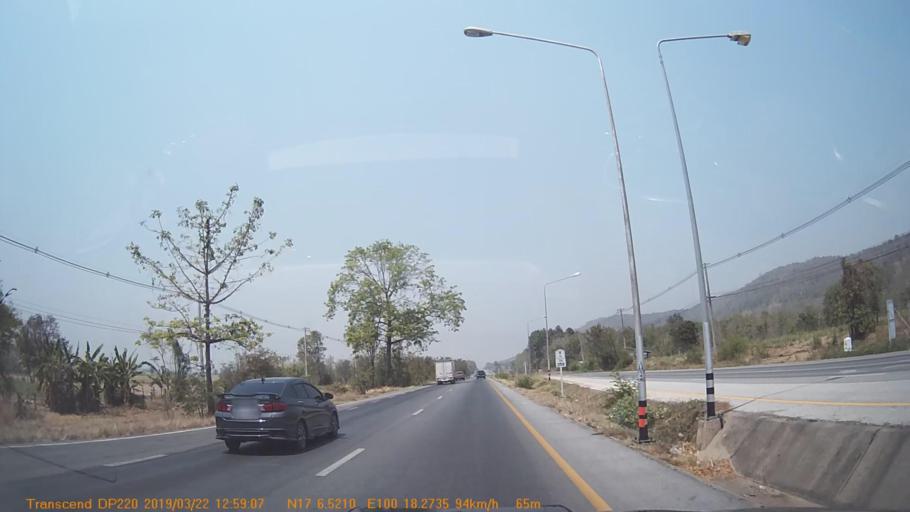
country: TH
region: Phitsanulok
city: Phrom Phiram
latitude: 17.1090
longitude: 100.3044
